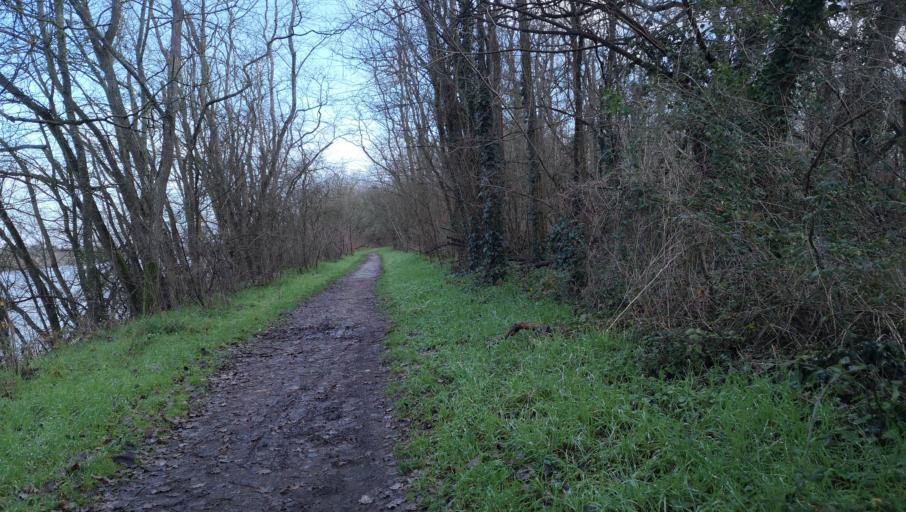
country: FR
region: Centre
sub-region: Departement du Loiret
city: Saint-Hilaire-Saint-Mesmin
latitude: 47.8726
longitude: 1.8239
